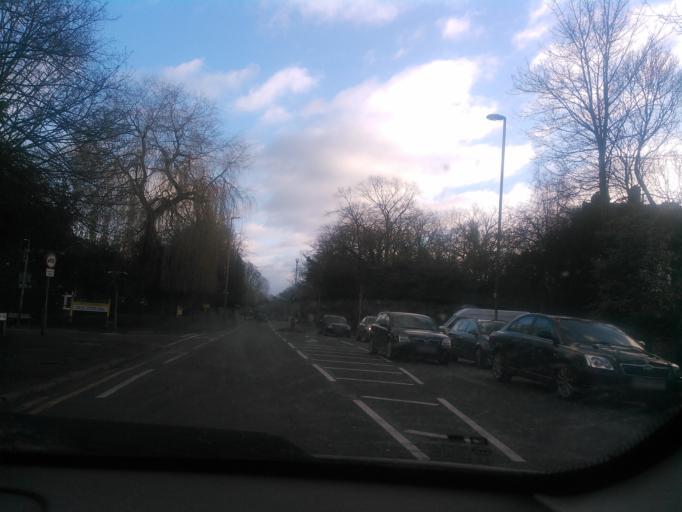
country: GB
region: England
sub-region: Leicestershire
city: Oadby
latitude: 52.6138
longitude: -1.1035
